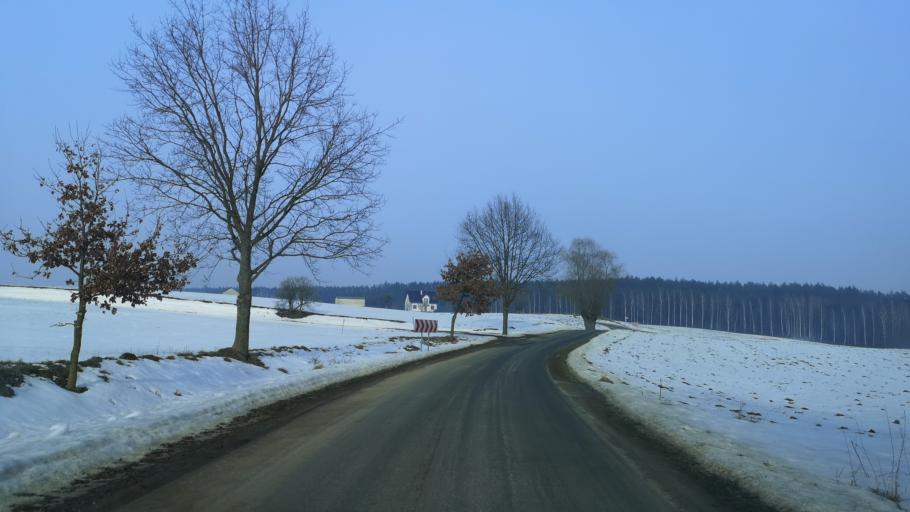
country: PL
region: Warmian-Masurian Voivodeship
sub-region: Powiat nowomiejski
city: Biskupiec
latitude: 53.5413
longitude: 19.3569
